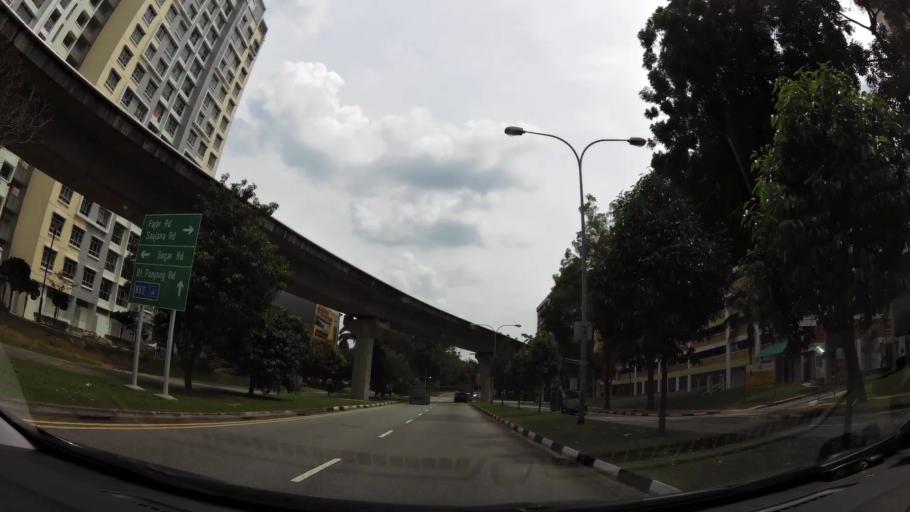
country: MY
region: Johor
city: Johor Bahru
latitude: 1.3868
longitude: 103.7709
